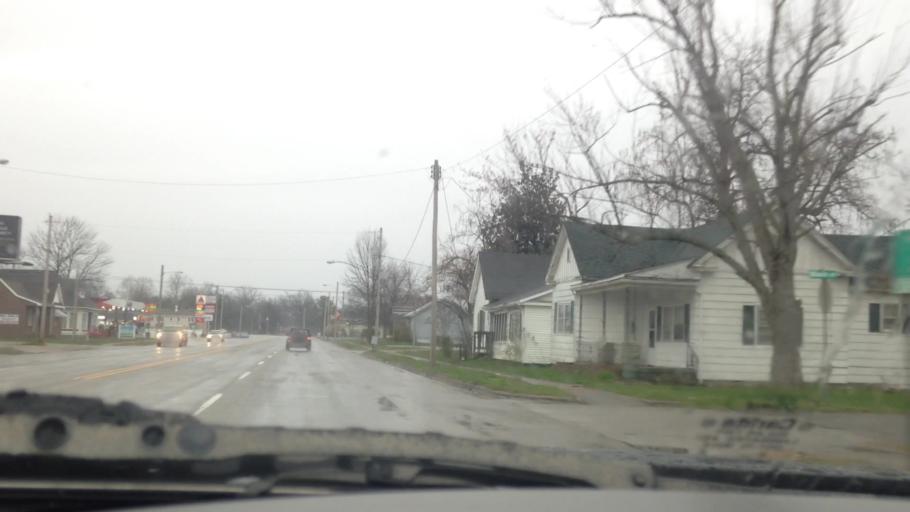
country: US
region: Illinois
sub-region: Massac County
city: Metropolis
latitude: 37.1454
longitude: -88.7193
